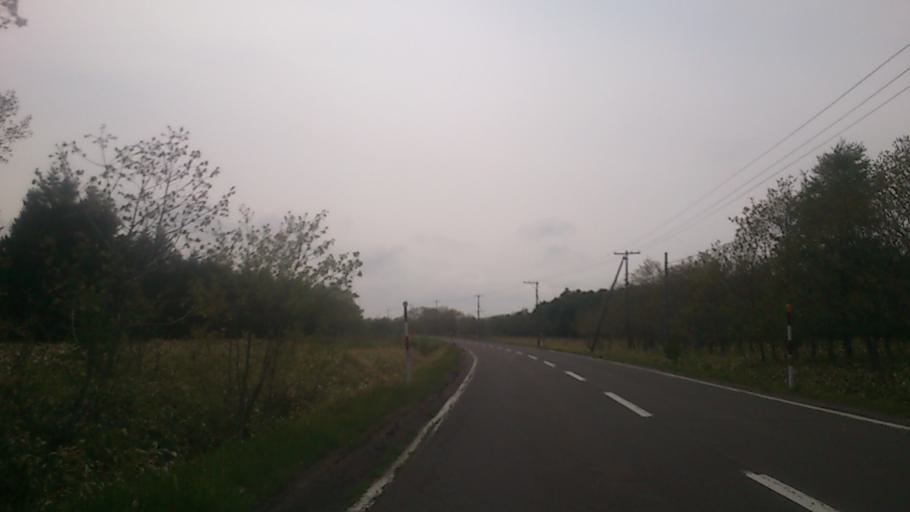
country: JP
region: Hokkaido
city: Nemuro
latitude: 43.2081
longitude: 145.3349
